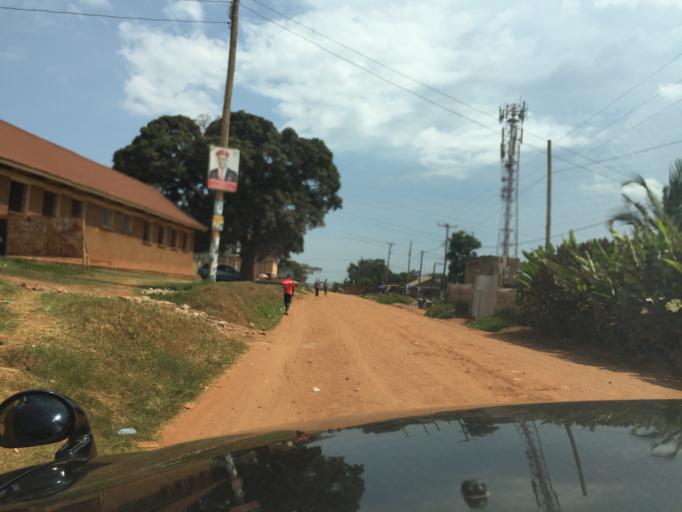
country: UG
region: Central Region
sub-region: Wakiso District
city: Kireka
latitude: 0.4056
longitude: 32.6201
